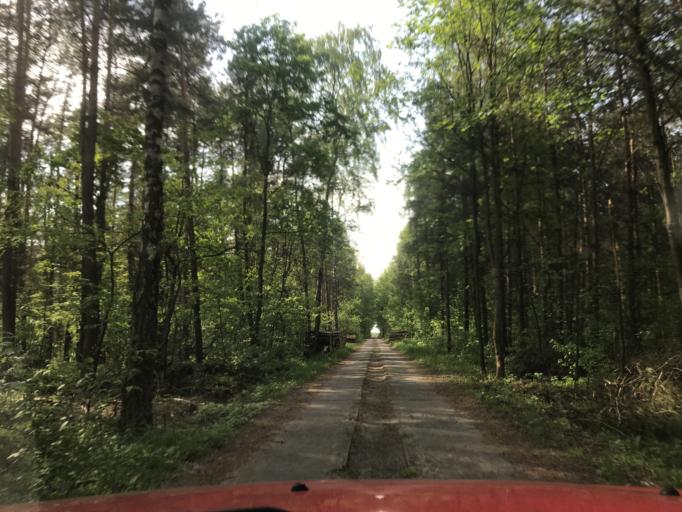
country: PL
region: Greater Poland Voivodeship
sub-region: Powiat kaliski
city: Stawiszyn
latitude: 51.9407
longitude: 18.1557
